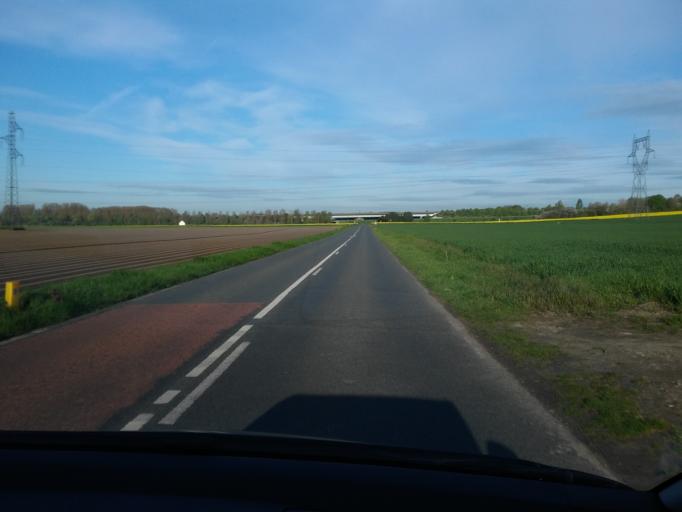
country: FR
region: Picardie
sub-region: Departement de l'Oise
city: Longueil-Sainte-Marie
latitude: 49.3495
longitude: 2.7124
